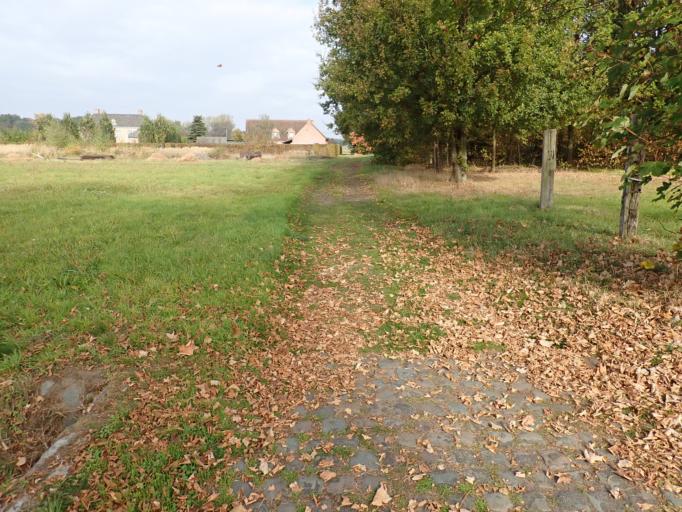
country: BE
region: Flanders
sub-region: Provincie Antwerpen
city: Berlaar
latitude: 51.1271
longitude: 4.6684
